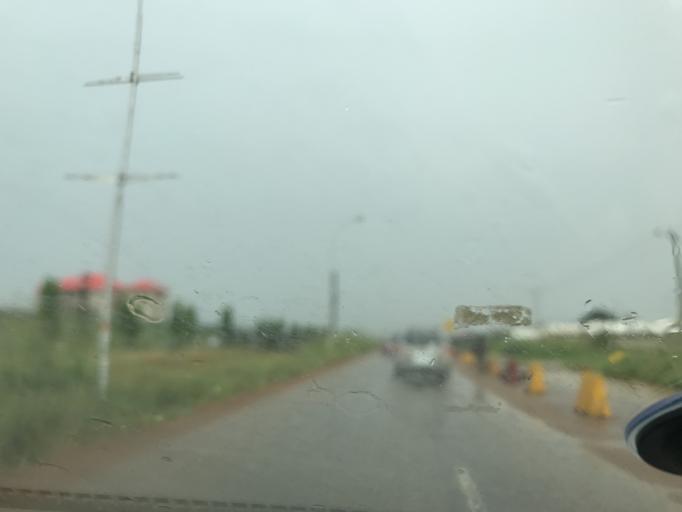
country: NG
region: Lagos
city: Oshodi
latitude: 6.5619
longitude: 3.3215
